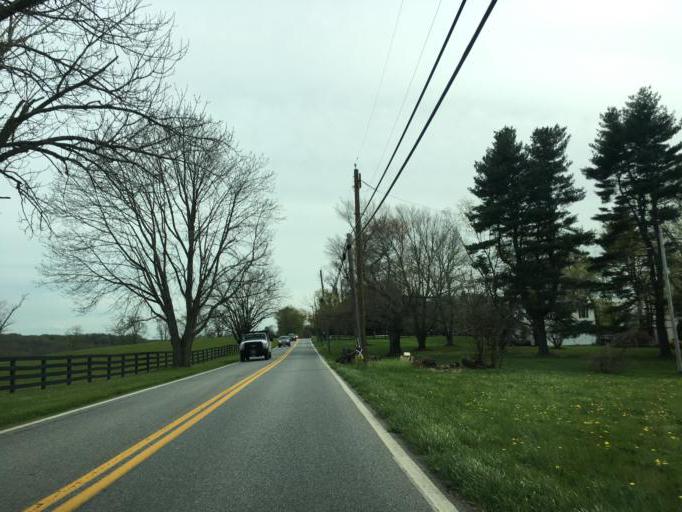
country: US
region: Maryland
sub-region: Baltimore County
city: Hunt Valley
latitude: 39.5439
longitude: -76.6121
